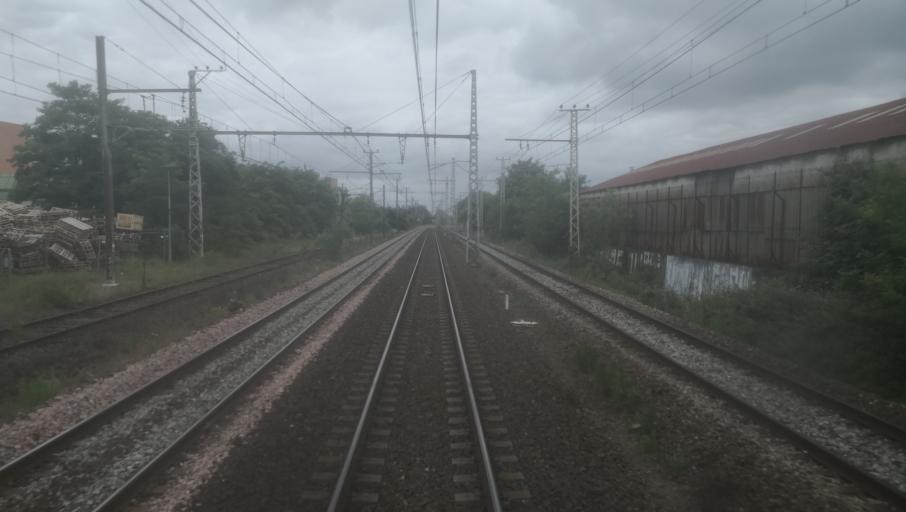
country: FR
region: Midi-Pyrenees
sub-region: Departement de la Haute-Garonne
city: Aucamville
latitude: 43.6443
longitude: 1.4300
